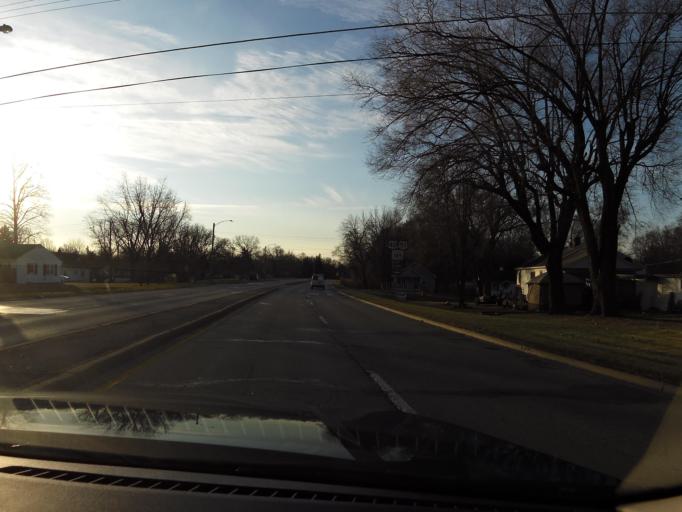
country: US
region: Illinois
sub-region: Fayette County
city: Vandalia
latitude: 38.9725
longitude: -89.0937
